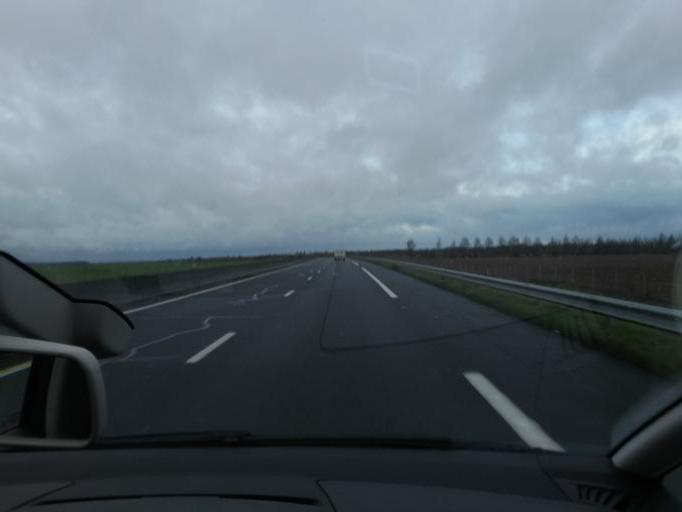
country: FR
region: Picardie
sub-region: Departement de la Somme
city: Villers-Bretonneux
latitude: 49.8604
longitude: 2.5789
